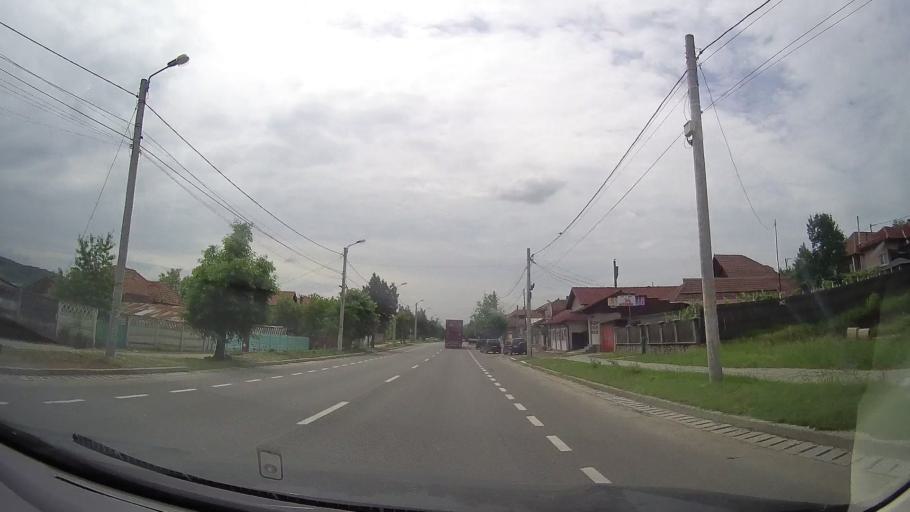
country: RO
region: Mehedinti
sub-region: Oras Strehaia
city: Strehaia
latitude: 44.6206
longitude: 23.1846
